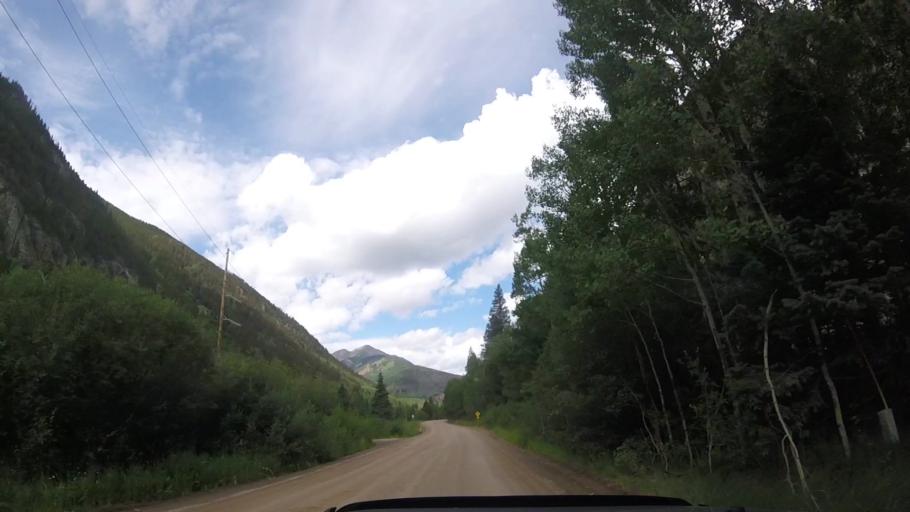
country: US
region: Colorado
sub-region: San Miguel County
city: Mountain Village
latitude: 37.8585
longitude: -107.8618
